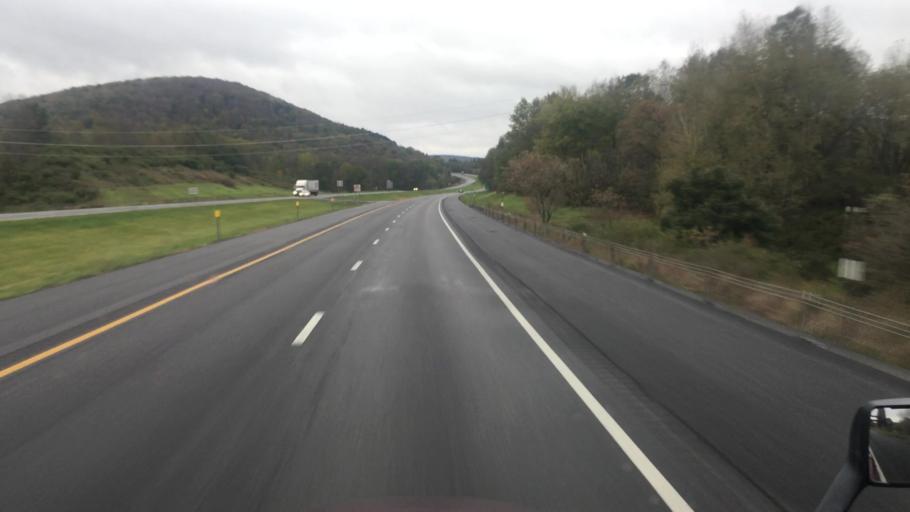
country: US
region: New York
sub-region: Otsego County
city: Unadilla
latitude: 42.3251
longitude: -75.2952
